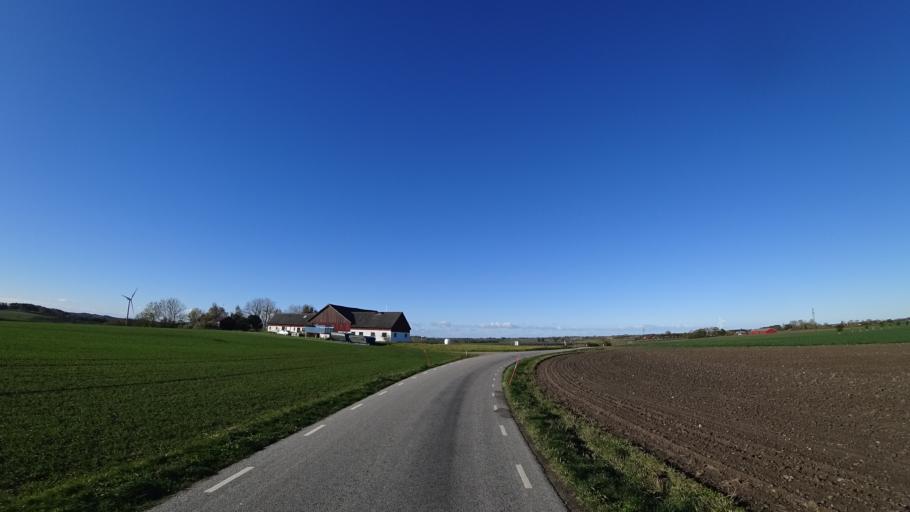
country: SE
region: Skane
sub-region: Svedala Kommun
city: Klagerup
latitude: 55.6158
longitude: 13.2858
